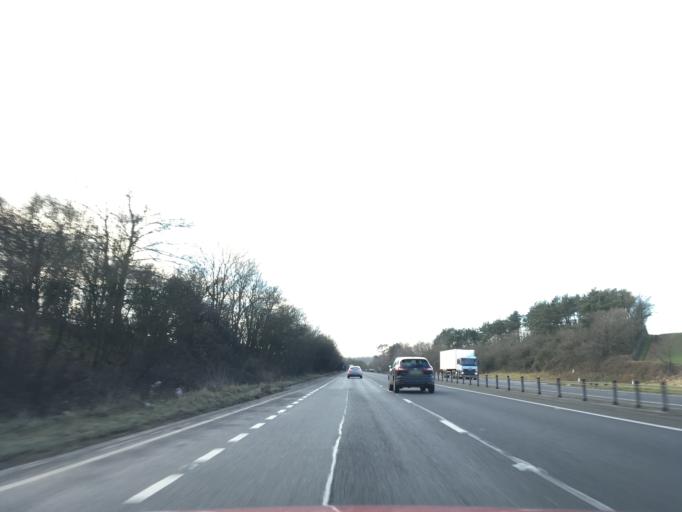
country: GB
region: Wales
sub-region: Monmouthshire
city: Llanarth
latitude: 51.7663
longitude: -2.8355
